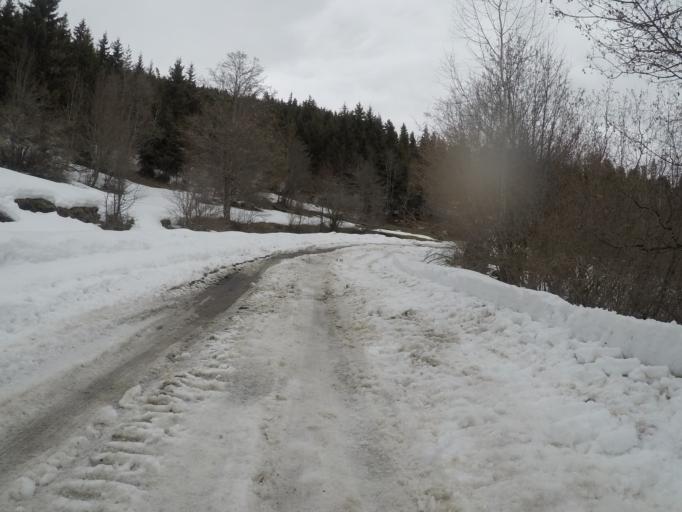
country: GE
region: Samtskhe-Javakheti
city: Adigeni
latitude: 41.6672
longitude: 42.6168
